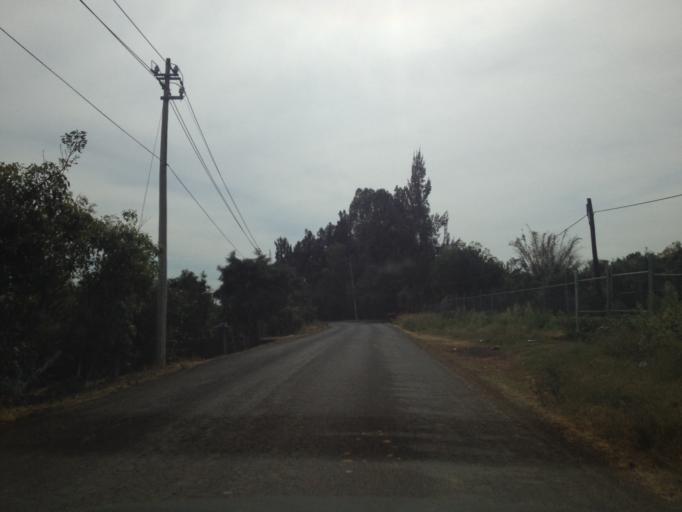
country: MX
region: Michoacan
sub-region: Ziracuaretiro
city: Patuan
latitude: 19.4283
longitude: -101.9236
